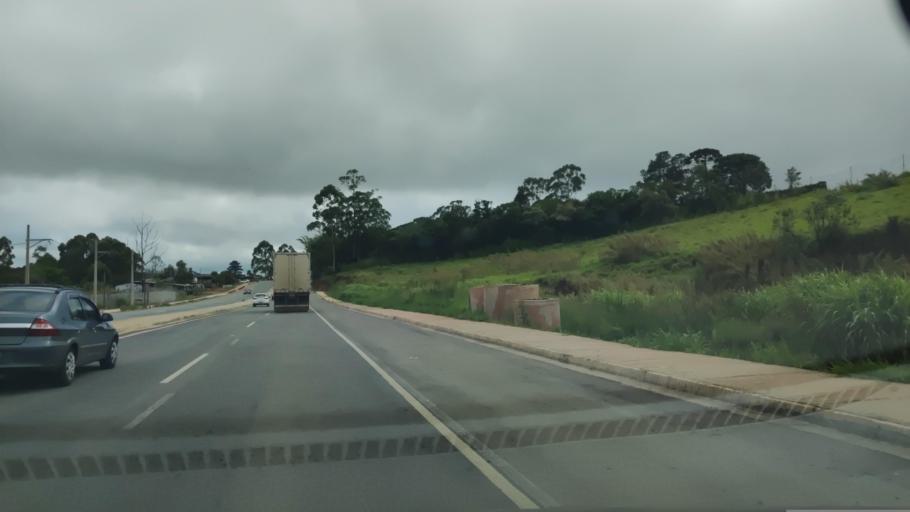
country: BR
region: Sao Paulo
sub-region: Vargem Grande Paulista
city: Vargem Grande Paulista
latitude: -23.6286
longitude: -47.0537
